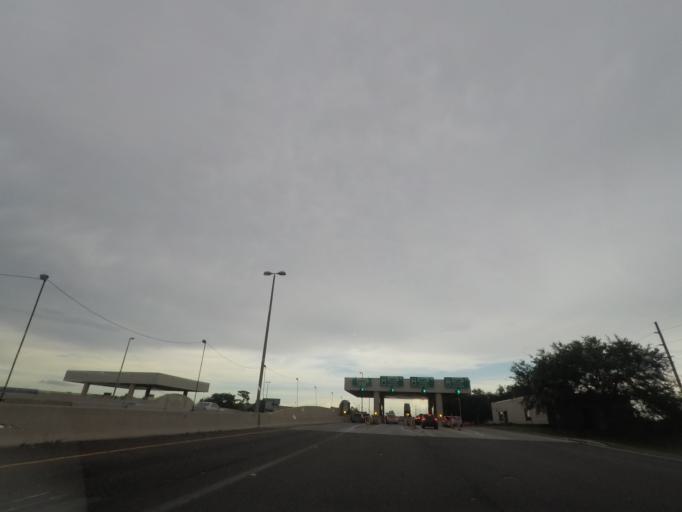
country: US
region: Florida
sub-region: Orange County
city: Sky Lake
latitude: 28.4444
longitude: -81.3825
